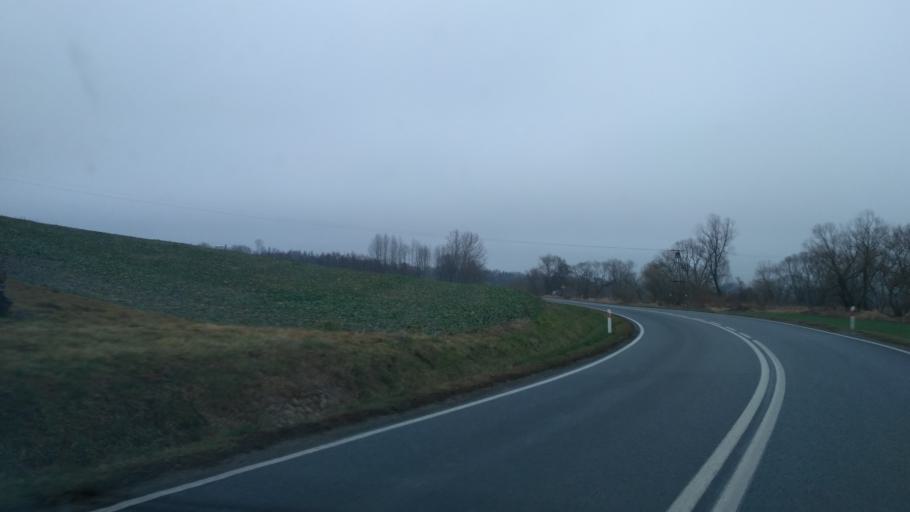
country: PL
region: Subcarpathian Voivodeship
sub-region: Powiat jaroslawski
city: Pruchnik
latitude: 49.9085
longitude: 22.5552
